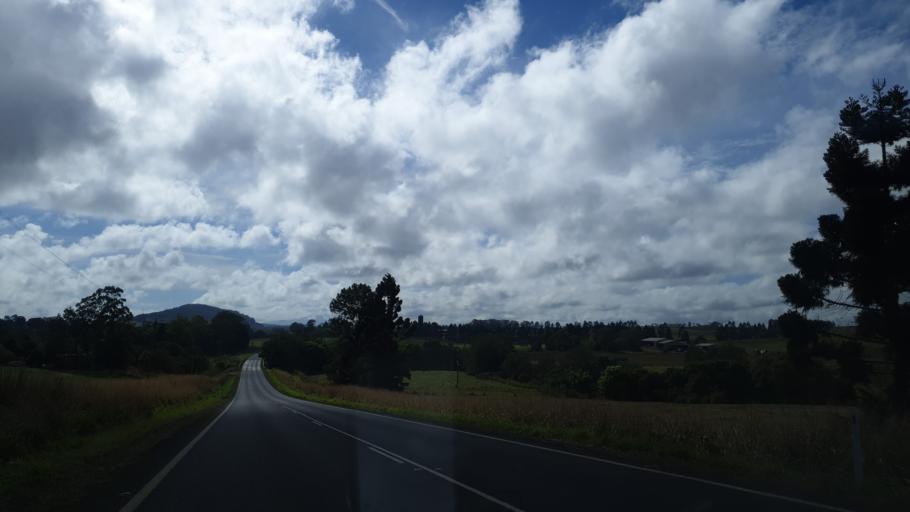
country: AU
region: Queensland
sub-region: Tablelands
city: Atherton
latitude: -17.2939
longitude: 145.5306
